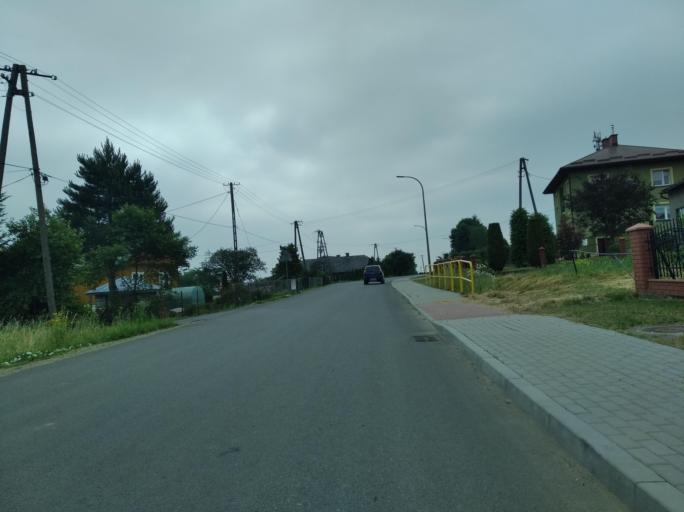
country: PL
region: Subcarpathian Voivodeship
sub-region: Powiat krosnienski
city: Rymanow
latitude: 49.6017
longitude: 21.9038
